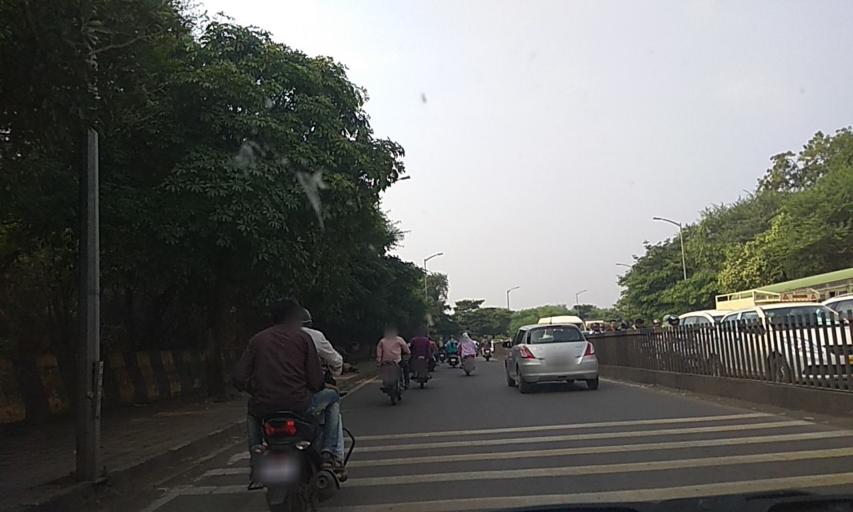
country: IN
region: Maharashtra
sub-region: Pune Division
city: Shivaji Nagar
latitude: 18.5440
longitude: 73.8765
